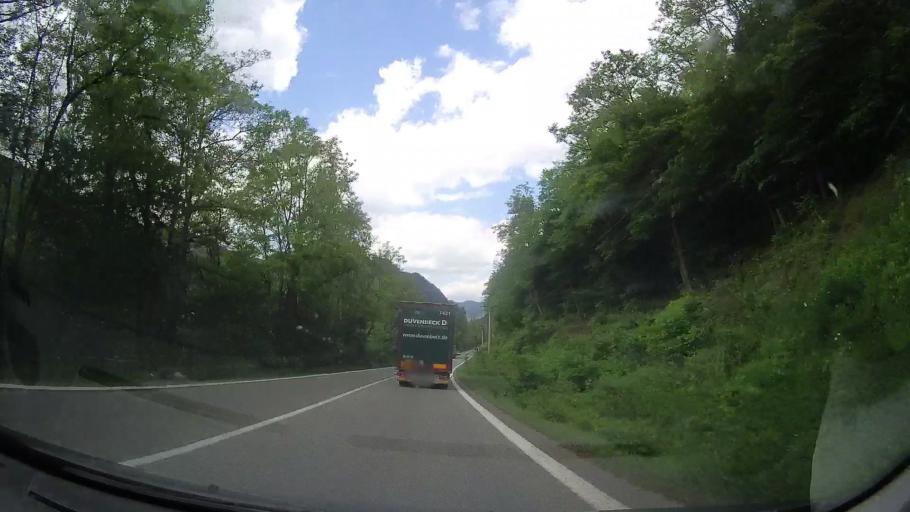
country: RO
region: Valcea
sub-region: Oras Calimanesti
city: Calimanesti
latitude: 45.2699
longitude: 24.3209
